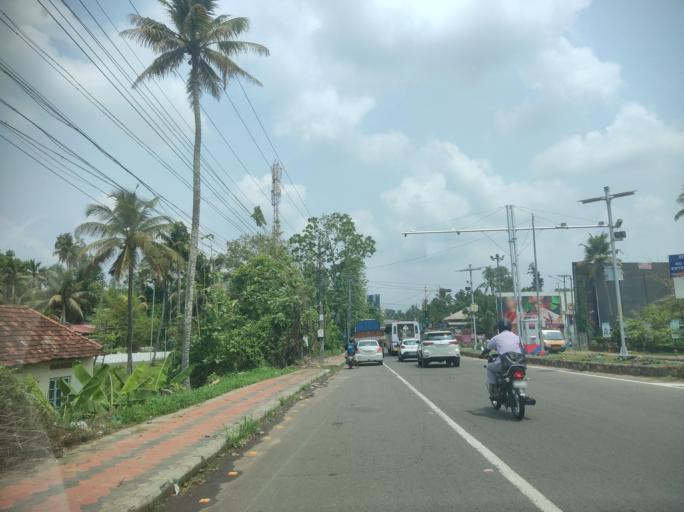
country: IN
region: Kerala
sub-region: Kottayam
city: Changanacheri
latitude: 9.4294
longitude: 76.5446
